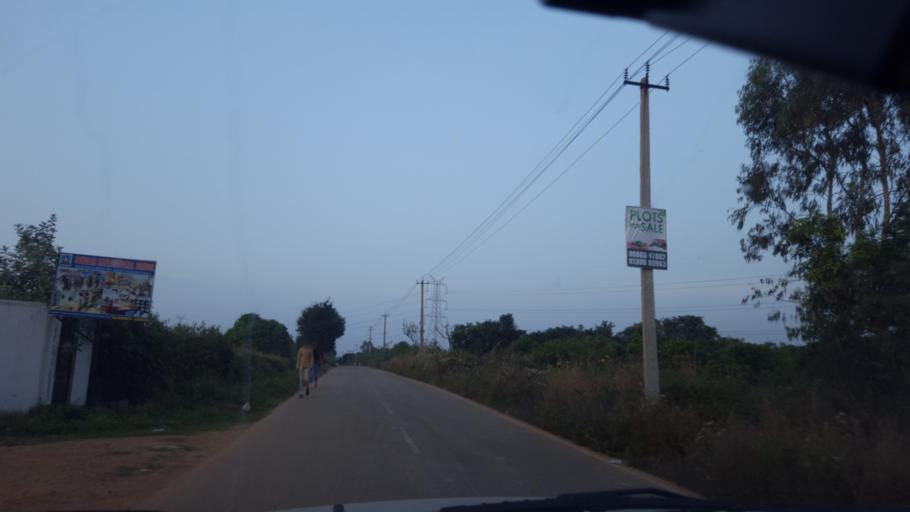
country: IN
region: Karnataka
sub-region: Bangalore Urban
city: Yelahanka
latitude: 13.0689
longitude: 77.6897
